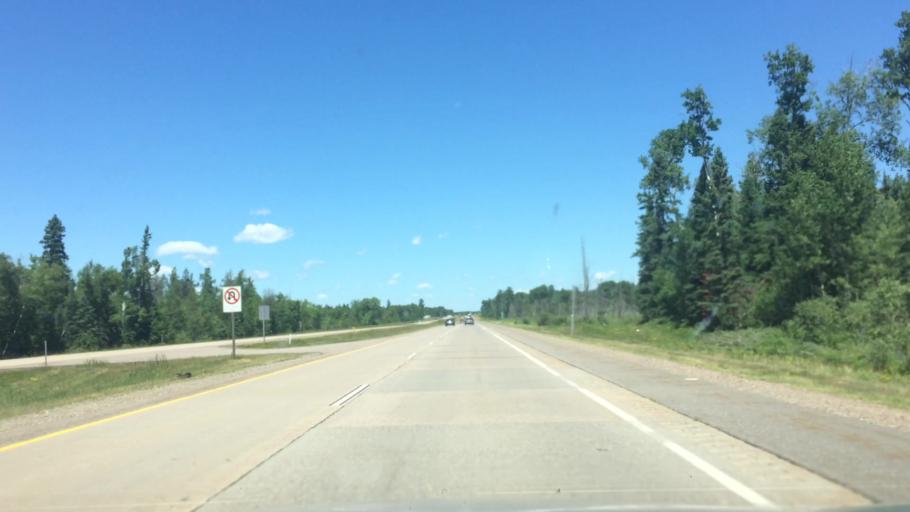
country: US
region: Wisconsin
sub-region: Lincoln County
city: Tomahawk
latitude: 45.3882
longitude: -89.6722
